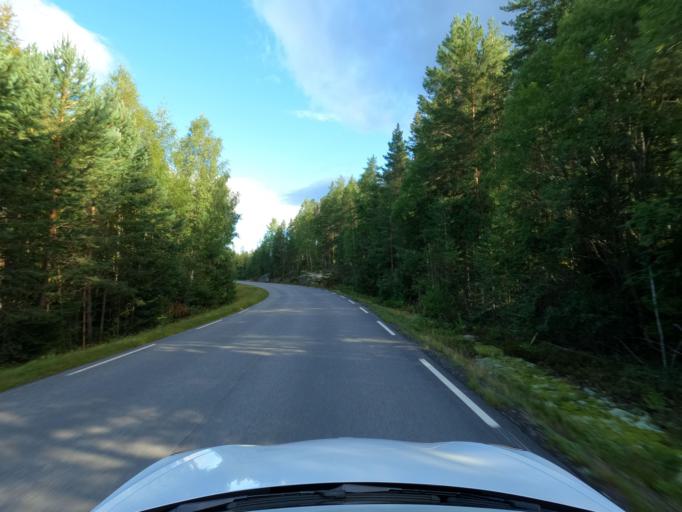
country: NO
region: Telemark
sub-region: Hjartdal
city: Sauland
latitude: 59.7917
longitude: 9.1009
